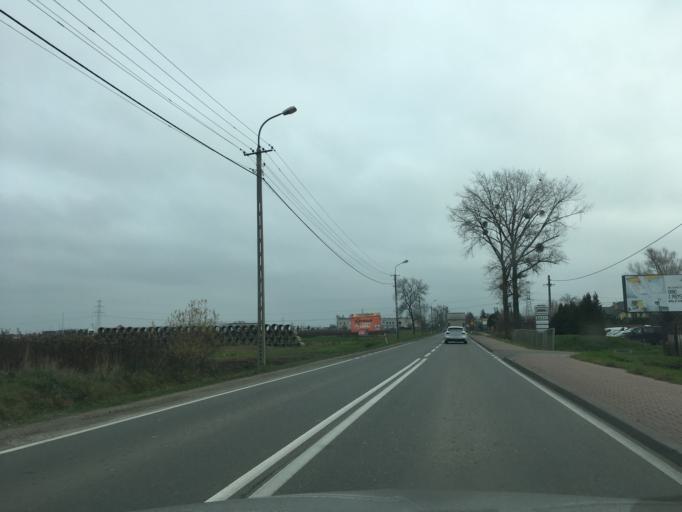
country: PL
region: Masovian Voivodeship
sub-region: Powiat piaseczynski
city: Lesznowola
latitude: 52.0829
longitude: 20.9614
